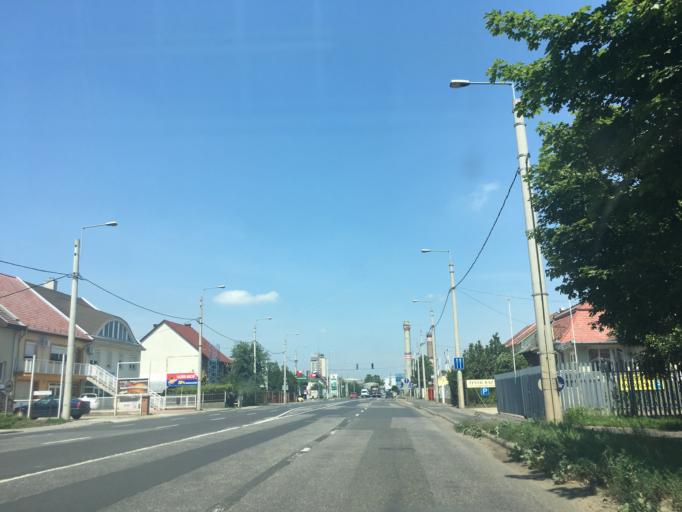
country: HU
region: Hajdu-Bihar
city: Debrecen
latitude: 47.5118
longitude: 21.6298
